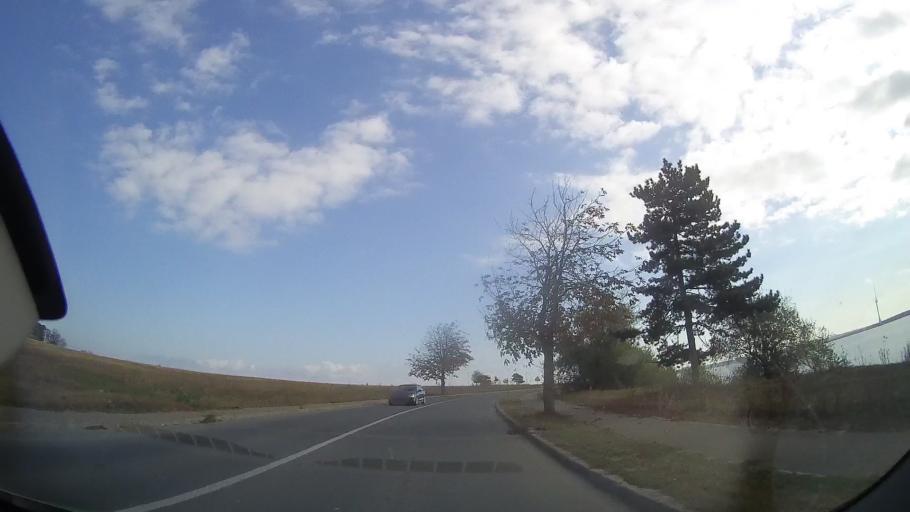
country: RO
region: Constanta
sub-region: Oras Techirghiol
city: Techirghiol
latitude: 44.0577
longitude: 28.6104
